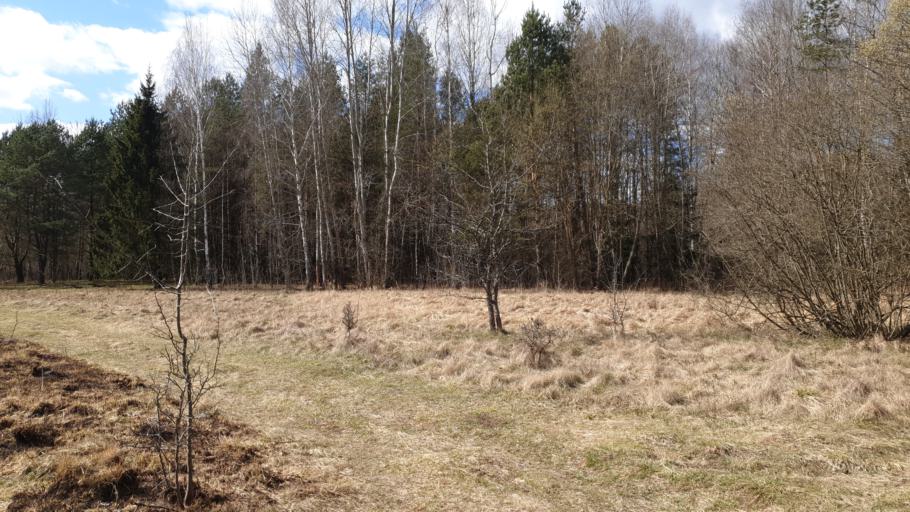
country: LT
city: Grigiskes
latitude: 54.7253
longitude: 25.0261
